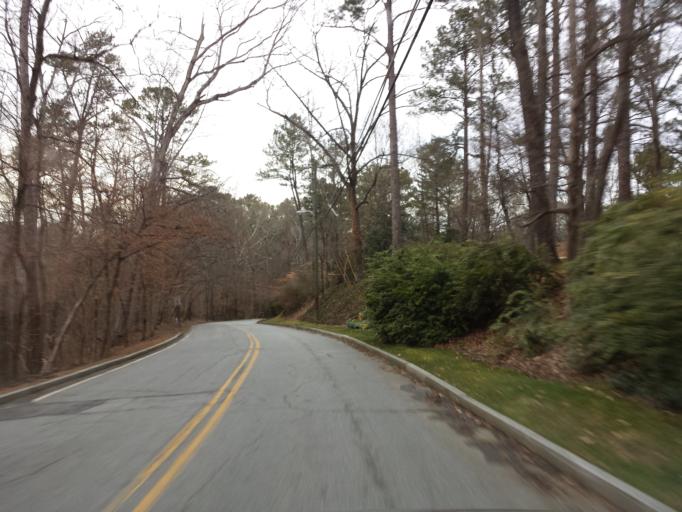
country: US
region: Georgia
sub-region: Cobb County
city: Vinings
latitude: 33.8752
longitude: -84.4348
